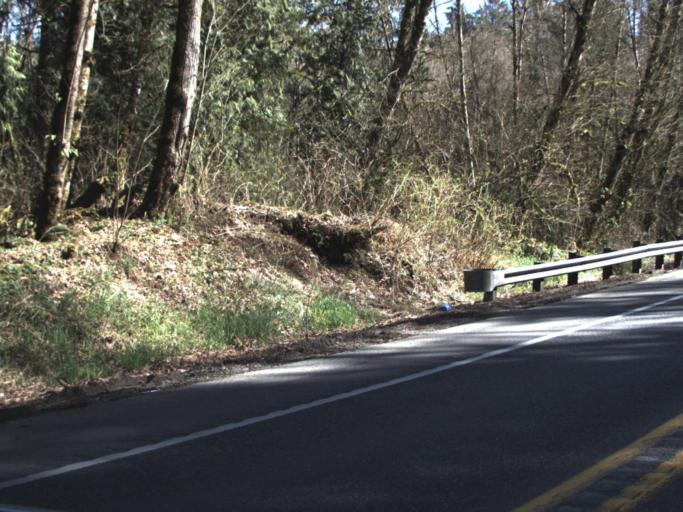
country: US
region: Washington
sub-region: King County
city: Black Diamond
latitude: 47.2680
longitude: -121.9920
